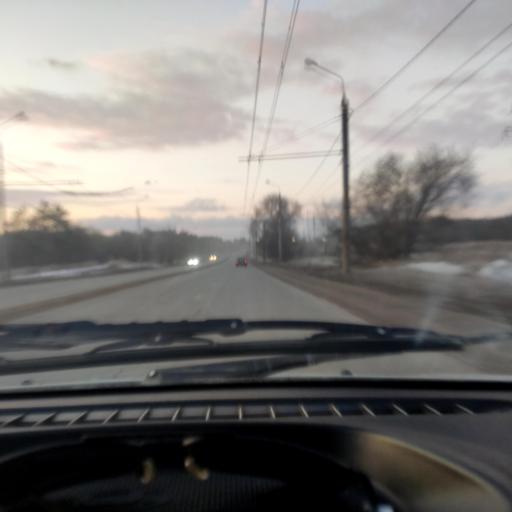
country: RU
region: Samara
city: Zhigulevsk
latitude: 53.5041
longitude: 49.5157
